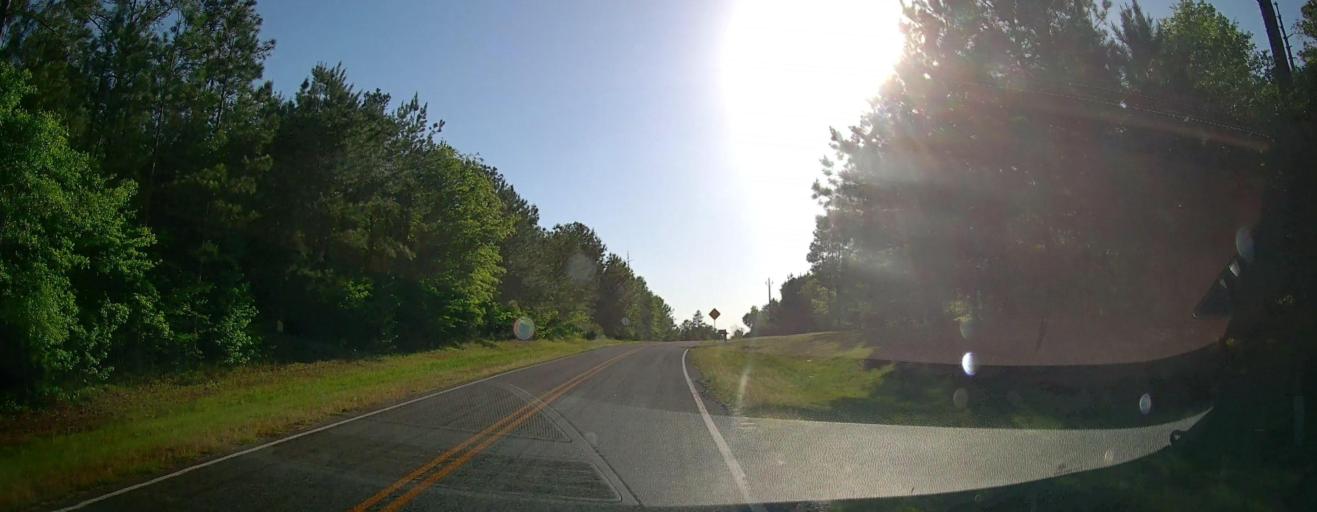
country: US
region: Georgia
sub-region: Houston County
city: Perry
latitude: 32.3945
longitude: -83.8349
